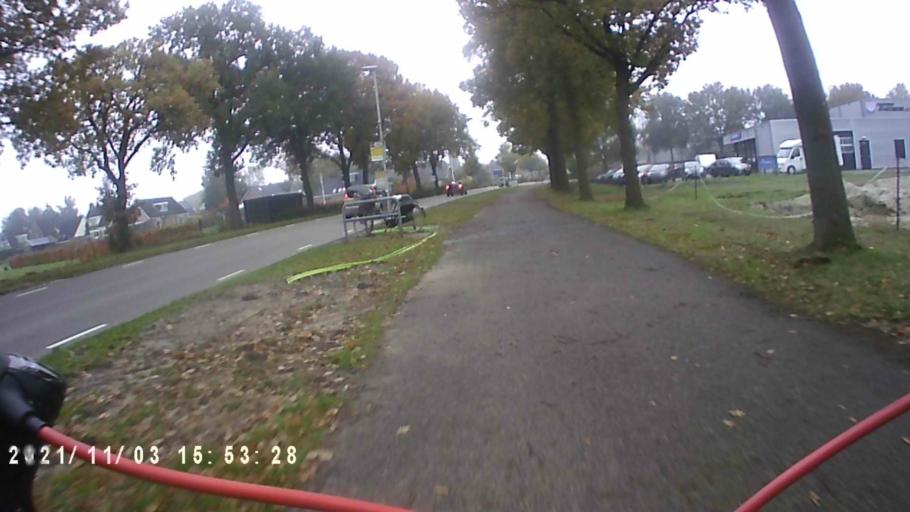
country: NL
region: Groningen
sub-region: Gemeente Leek
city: Leek
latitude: 53.0713
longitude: 6.3321
